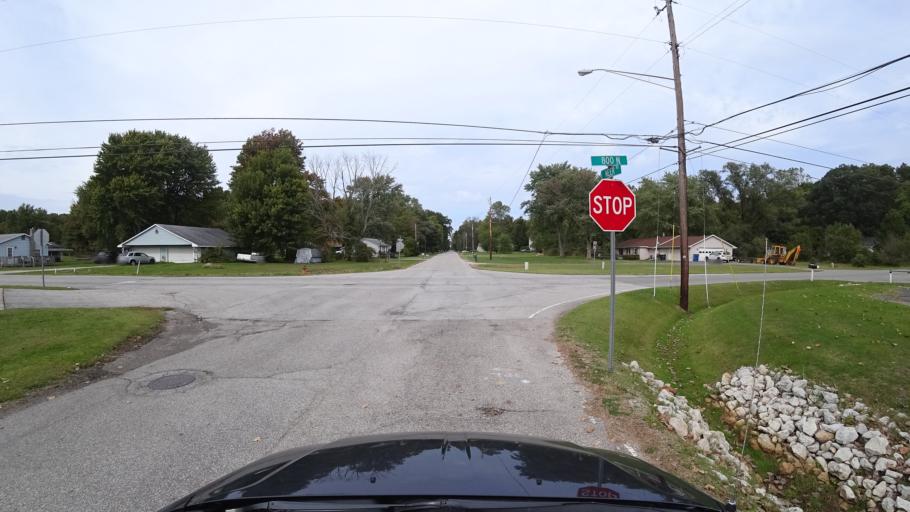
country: US
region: Indiana
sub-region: LaPorte County
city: Long Beach
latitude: 41.7233
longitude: -86.8162
